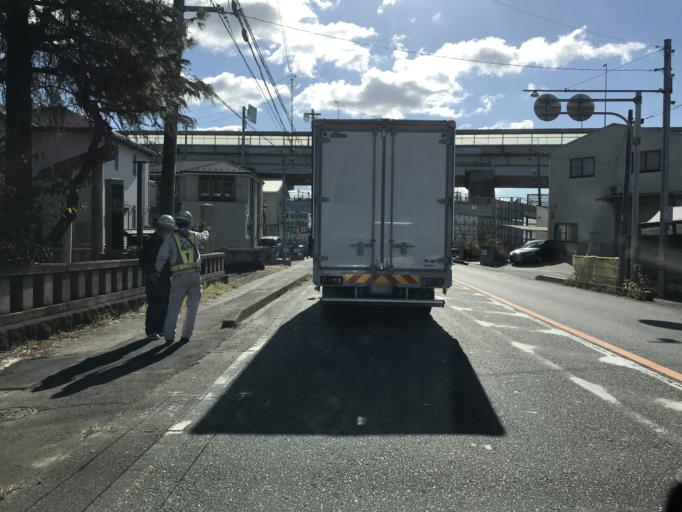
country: JP
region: Aichi
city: Inazawa
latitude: 35.2211
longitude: 136.8424
